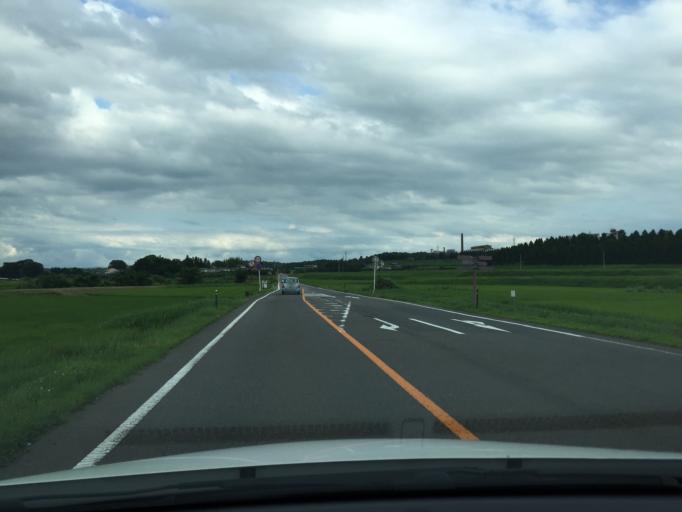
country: JP
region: Fukushima
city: Sukagawa
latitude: 37.2017
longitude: 140.2738
